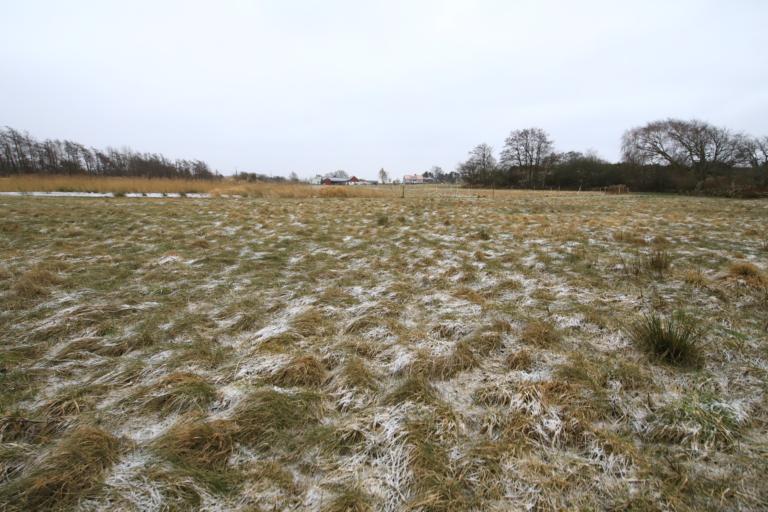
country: SE
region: Halland
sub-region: Varbergs Kommun
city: Veddige
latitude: 57.2139
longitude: 12.2192
